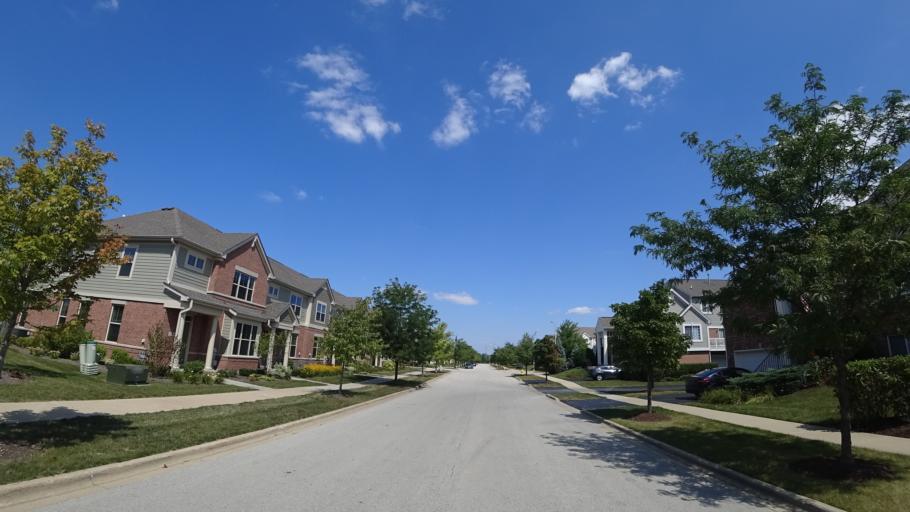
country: US
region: Illinois
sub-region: Cook County
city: Orland Park
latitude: 41.6335
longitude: -87.8504
